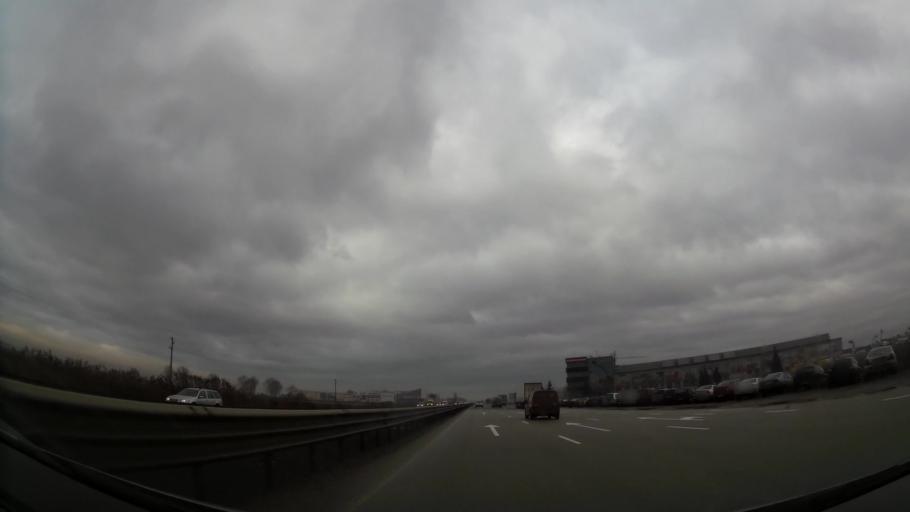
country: BG
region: Sofia-Capital
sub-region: Stolichna Obshtina
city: Sofia
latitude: 42.6744
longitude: 23.4555
